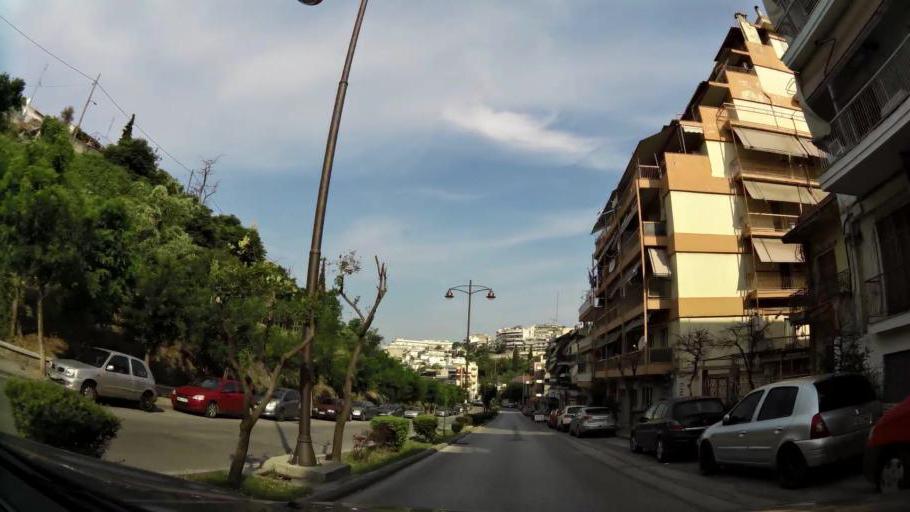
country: GR
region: Central Macedonia
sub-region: Nomos Thessalonikis
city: Sykies
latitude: 40.6450
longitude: 22.9464
